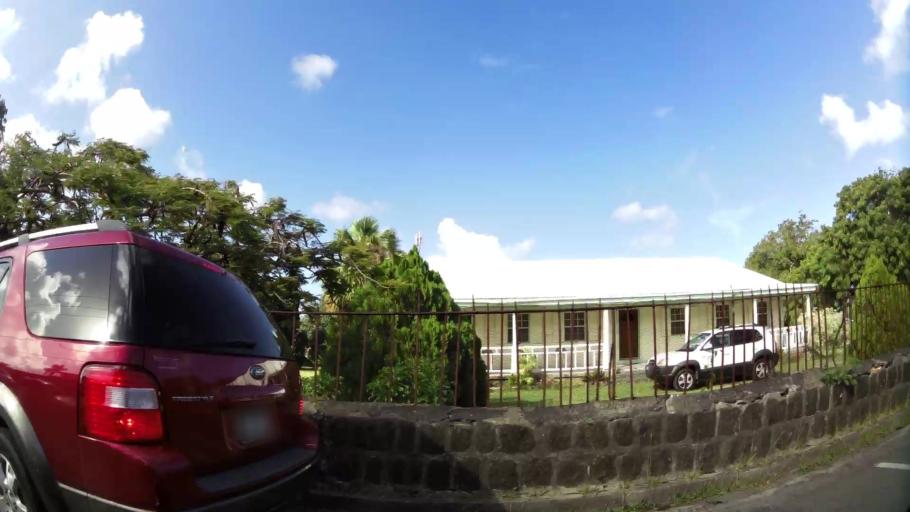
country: KN
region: Saint Paul Charlestown
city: Charlestown
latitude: 17.1393
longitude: -62.6273
